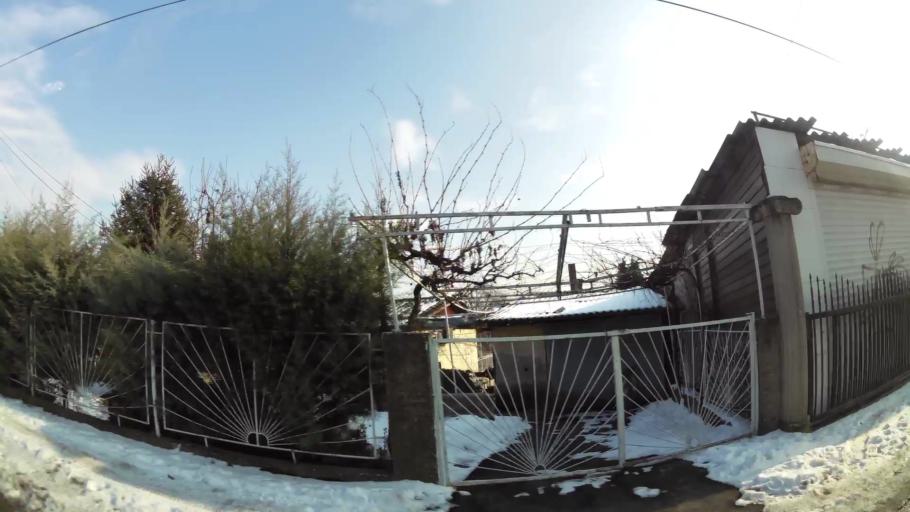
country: MK
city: Creshevo
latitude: 42.0138
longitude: 21.5047
